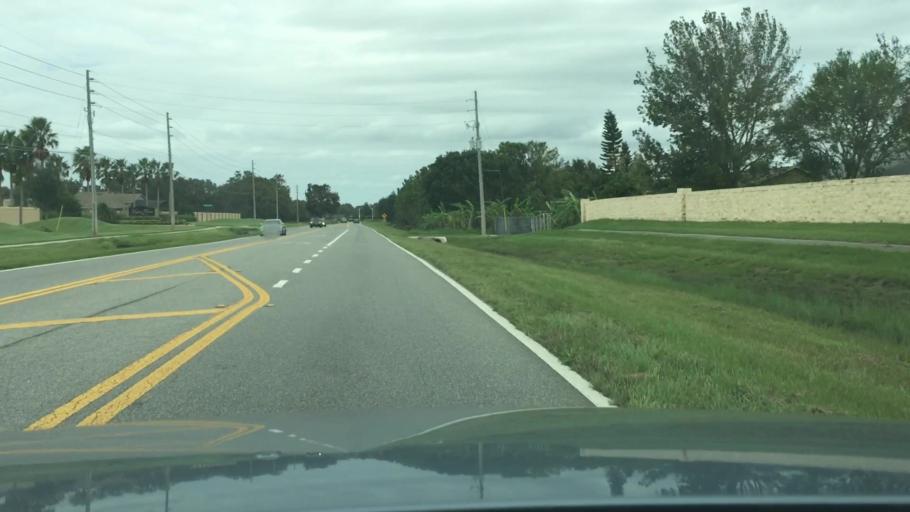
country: US
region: Florida
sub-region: Osceola County
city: Saint Cloud
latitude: 28.2066
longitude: -81.3008
